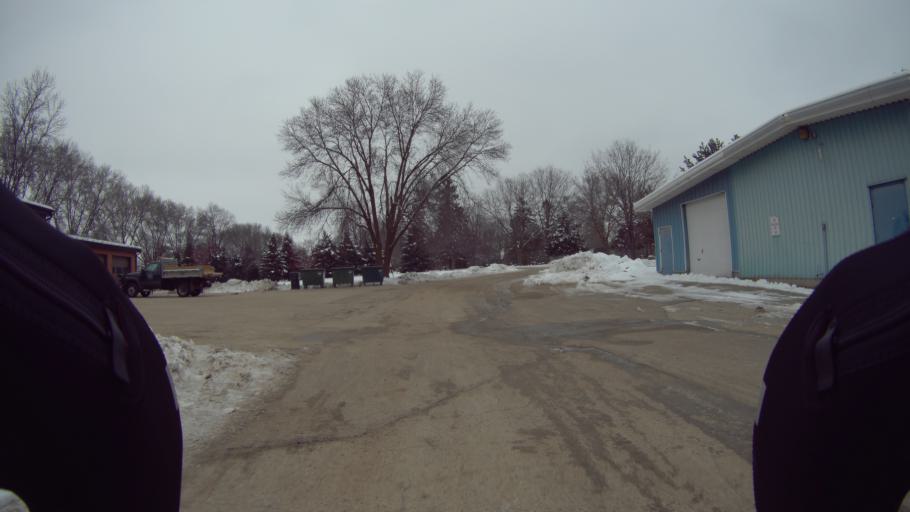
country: US
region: Wisconsin
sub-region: Dane County
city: Shorewood Hills
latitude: 43.0614
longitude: -89.4372
